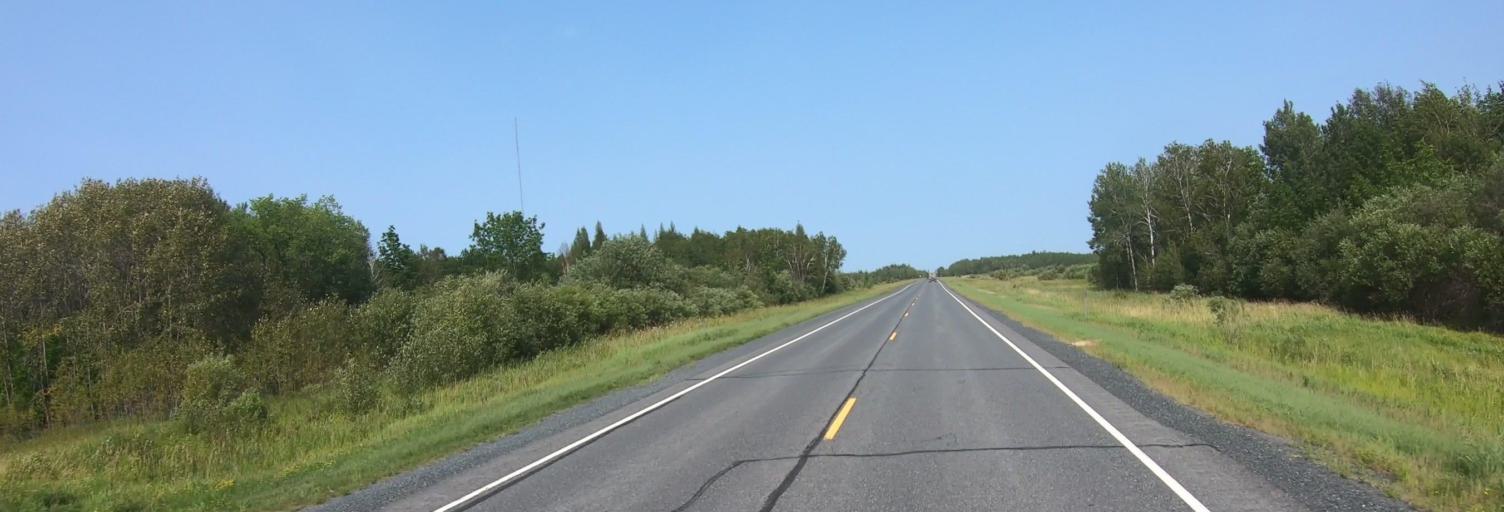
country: US
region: Minnesota
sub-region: Koochiching County
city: International Falls
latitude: 48.5558
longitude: -93.8182
